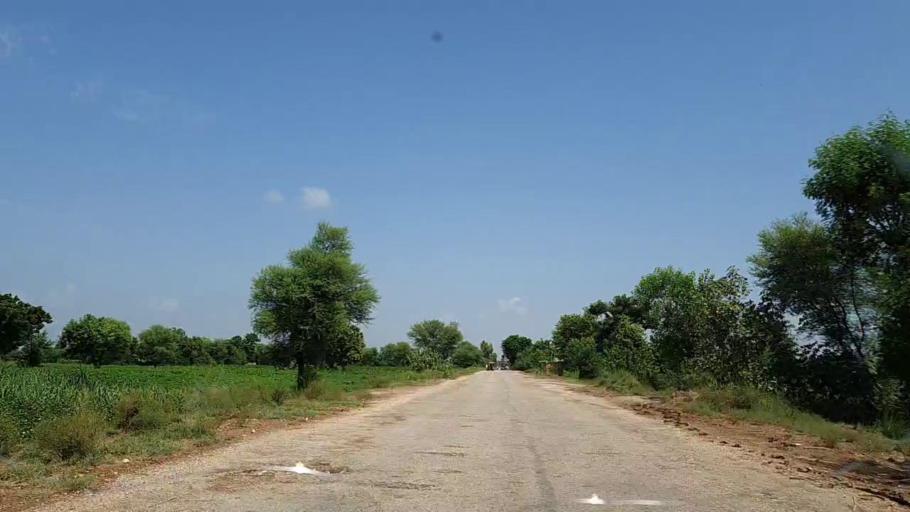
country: PK
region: Sindh
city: Pad Idan
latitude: 26.8024
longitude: 68.2206
